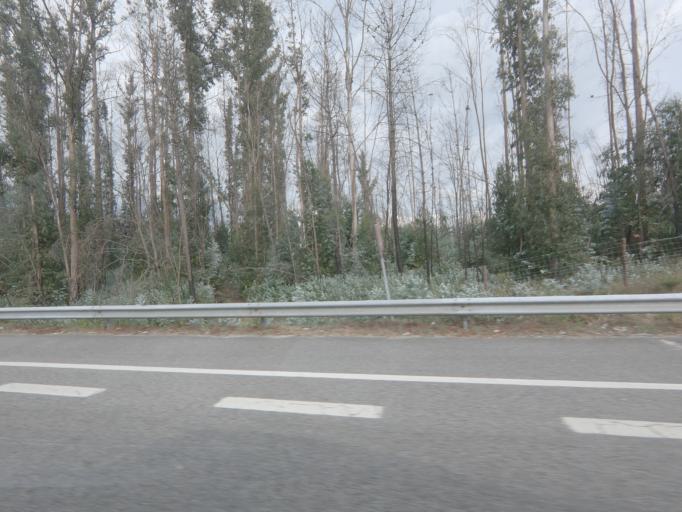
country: PT
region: Viseu
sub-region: Santa Comba Dao
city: Santa Comba Dao
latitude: 40.4416
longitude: -8.1082
